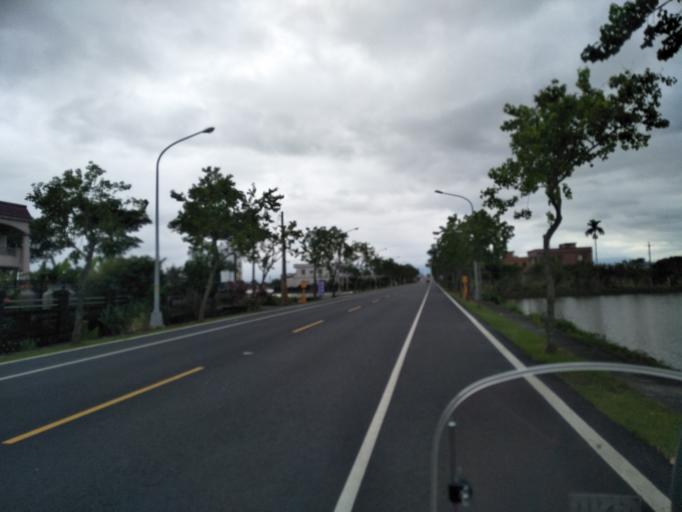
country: TW
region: Taiwan
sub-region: Yilan
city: Yilan
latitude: 24.8138
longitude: 121.7937
